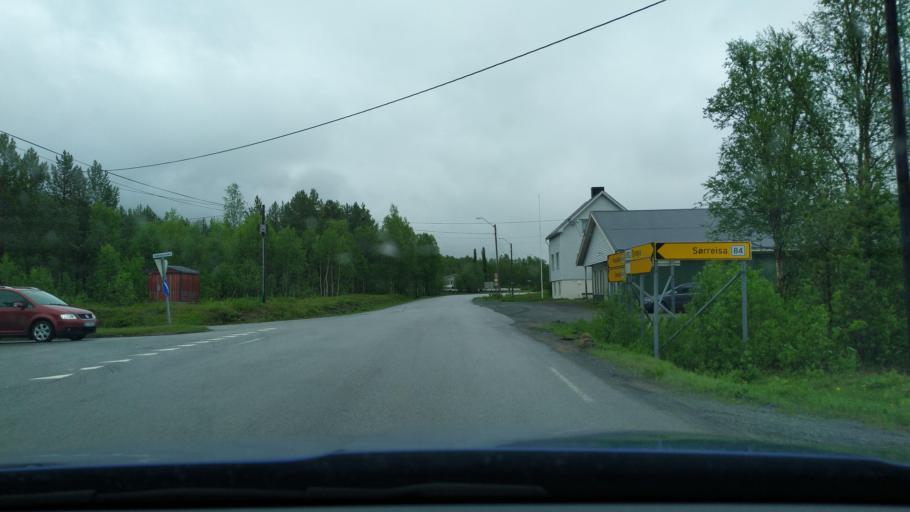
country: NO
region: Troms
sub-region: Dyroy
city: Brostadbotn
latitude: 69.0633
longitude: 17.7357
